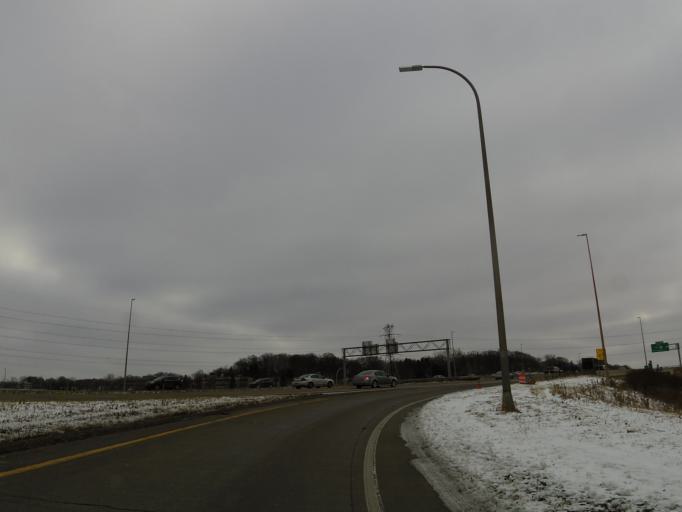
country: US
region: Minnesota
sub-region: Hennepin County
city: Minnetonka Mills
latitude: 44.9722
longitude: -93.4610
